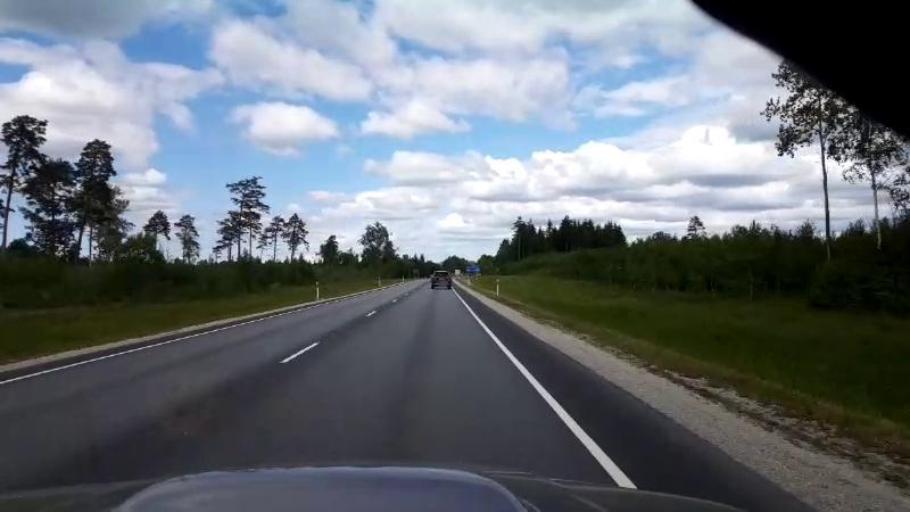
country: EE
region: Harju
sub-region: Nissi vald
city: Riisipere
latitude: 59.0749
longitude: 24.4535
